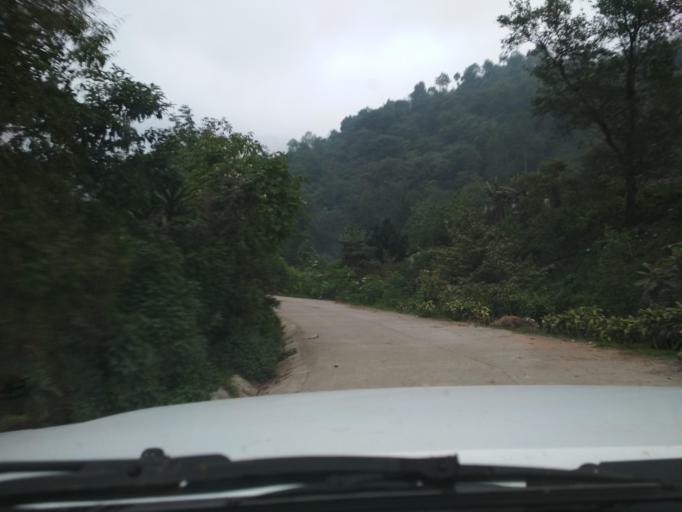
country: MX
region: Veracruz
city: La Perla
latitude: 18.9298
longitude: -97.1483
